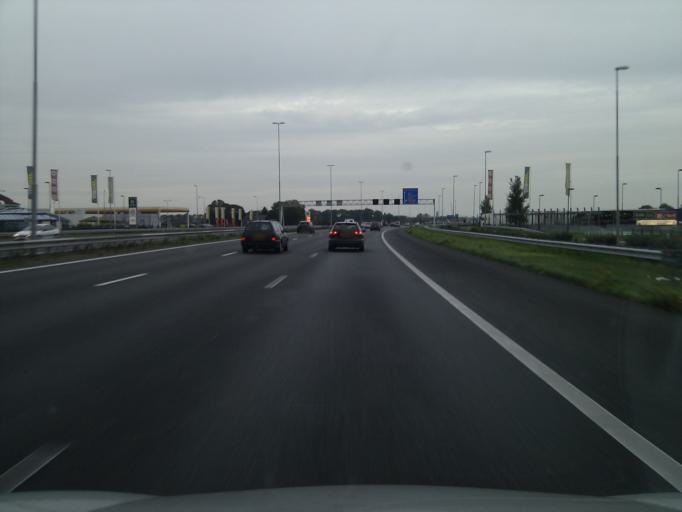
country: NL
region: Gelderland
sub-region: Gemeente Maasdriel
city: Hedel
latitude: 51.7755
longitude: 5.2596
